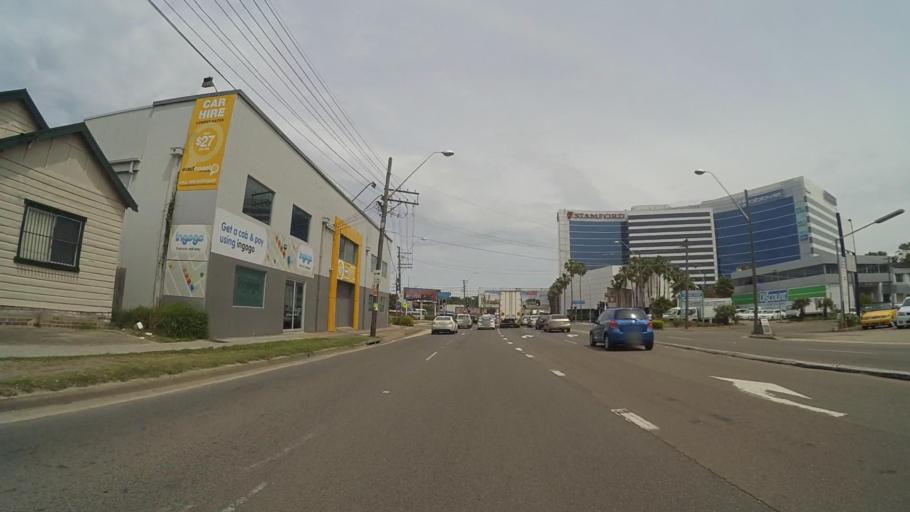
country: AU
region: New South Wales
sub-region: Botany Bay
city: Mascot
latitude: -33.9300
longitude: 151.1868
